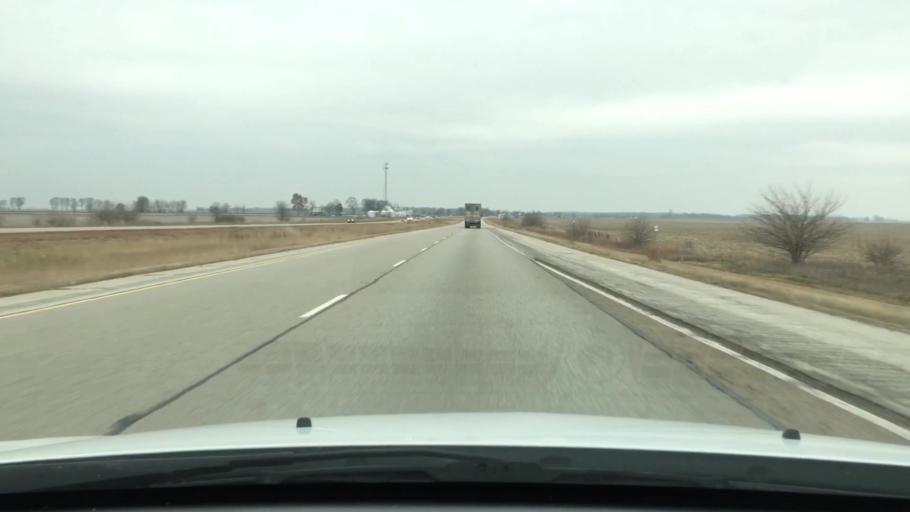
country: US
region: Illinois
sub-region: Logan County
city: Atlanta
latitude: 40.3169
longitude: -89.1593
